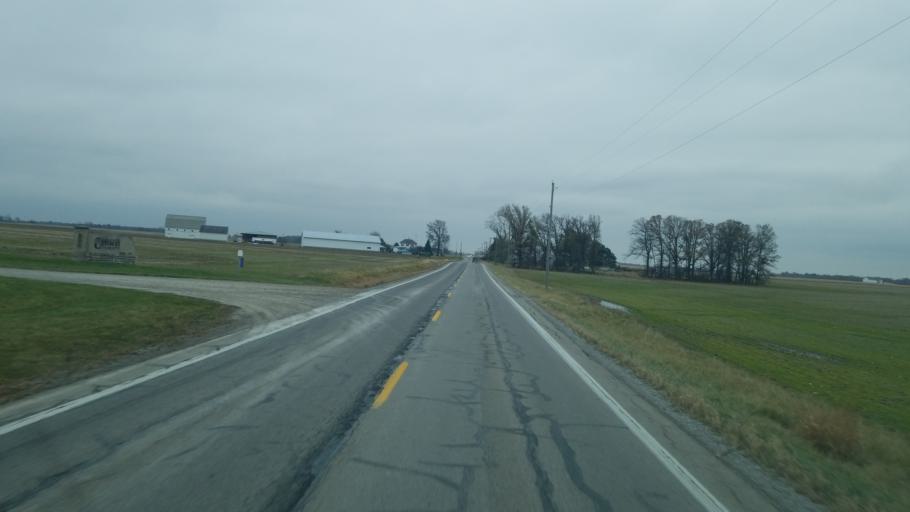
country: US
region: Ohio
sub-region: Huron County
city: Bellevue
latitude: 41.1334
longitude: -82.8555
